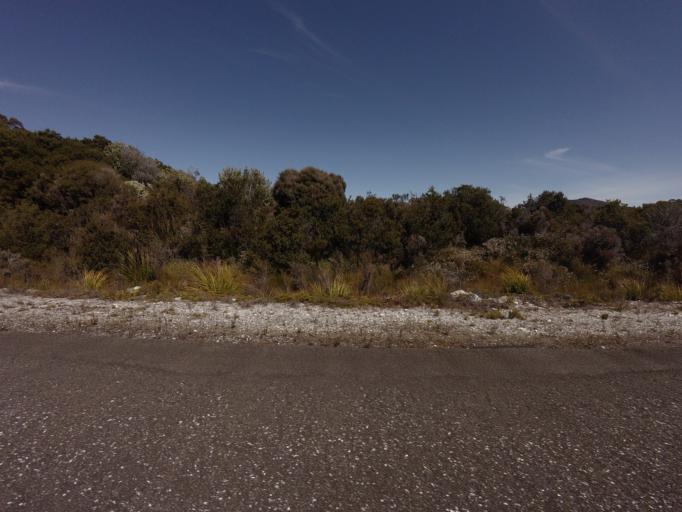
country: AU
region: Tasmania
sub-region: Huon Valley
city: Geeveston
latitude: -42.8328
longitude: 146.1506
